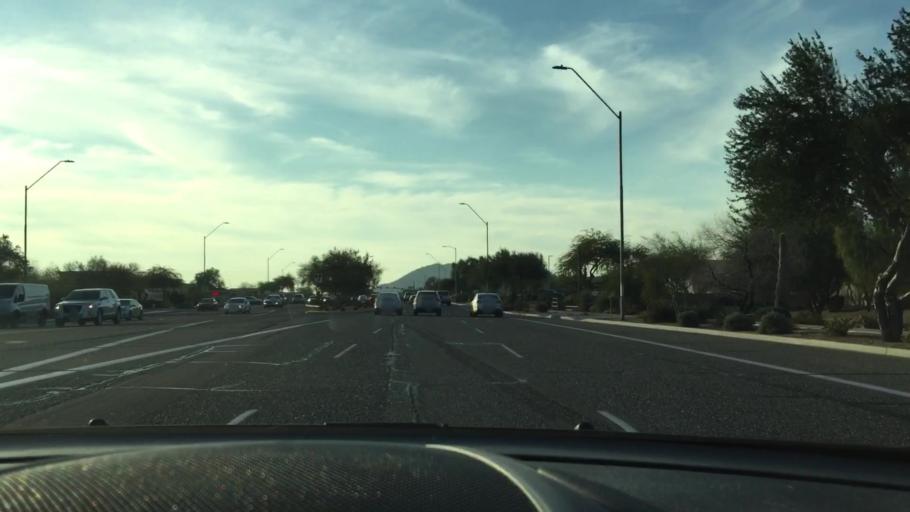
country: US
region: Arizona
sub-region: Maricopa County
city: Sun City
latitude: 33.7123
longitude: -112.1988
